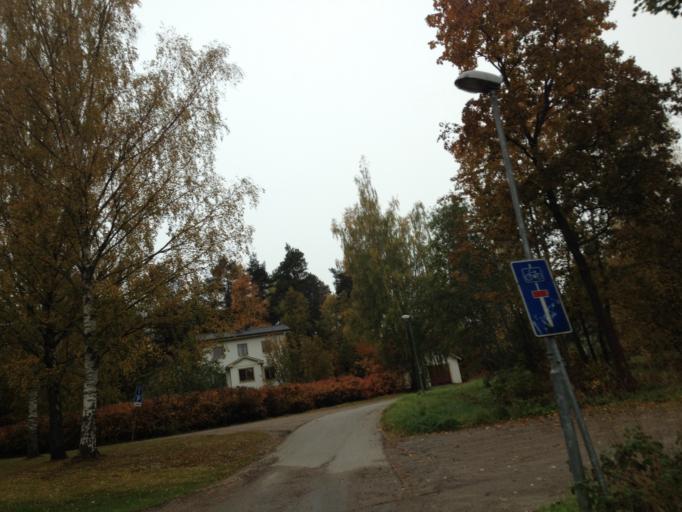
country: SE
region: Gaevleborg
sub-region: Bollnas Kommun
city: Bollnas
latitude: 61.3471
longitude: 16.3823
